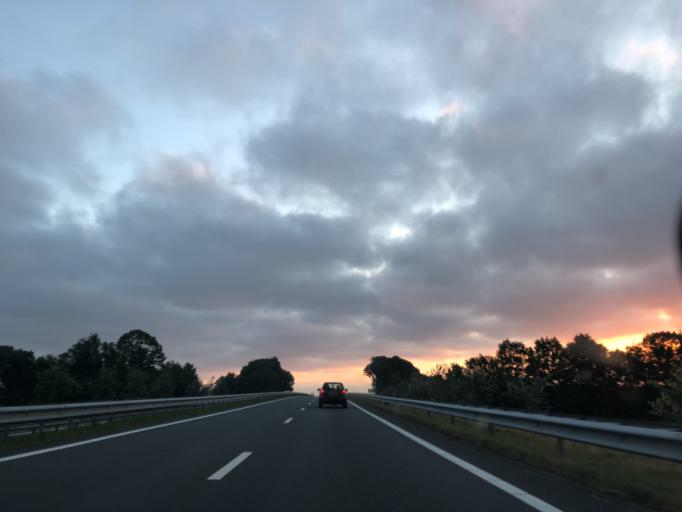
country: NL
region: Groningen
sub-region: Gemeente Veendam
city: Veendam
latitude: 53.0907
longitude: 6.8904
